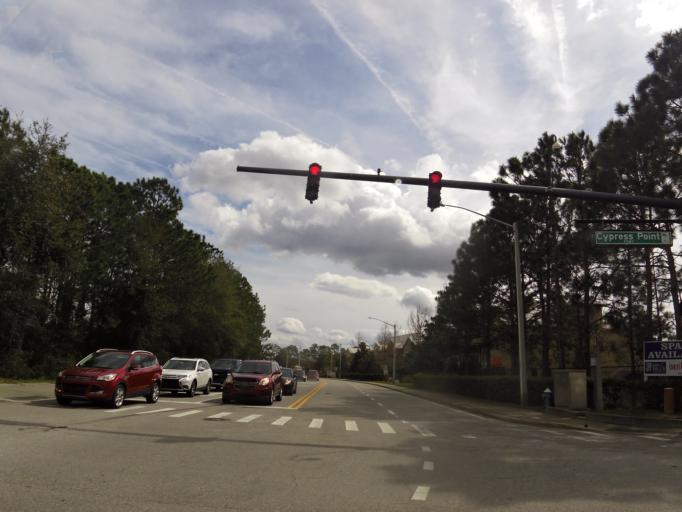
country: US
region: Florida
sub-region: Flagler County
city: Palm Coast
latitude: 29.5496
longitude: -81.2277
